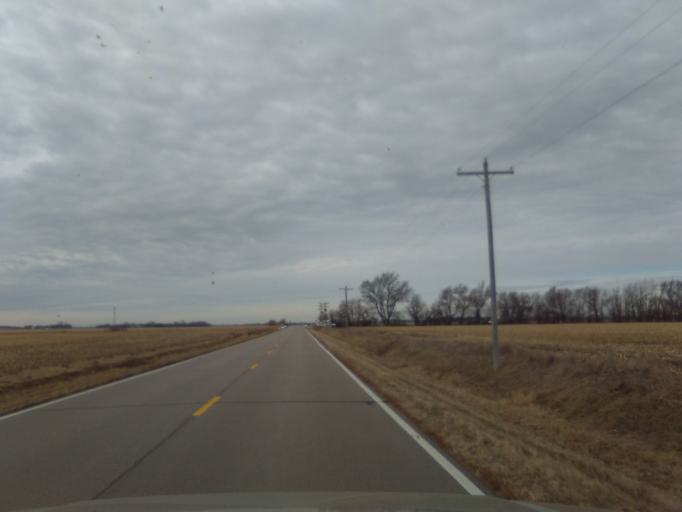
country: US
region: Nebraska
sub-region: Hall County
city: Wood River
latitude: 40.7711
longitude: -98.4326
